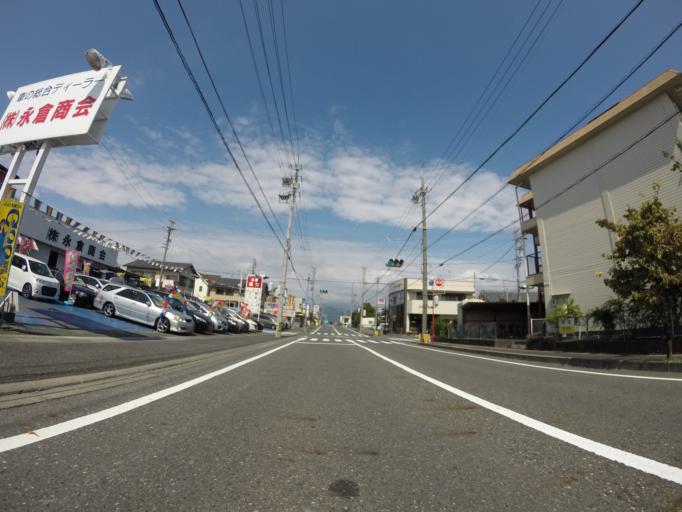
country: JP
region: Shizuoka
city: Shizuoka-shi
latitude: 35.0088
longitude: 138.4715
